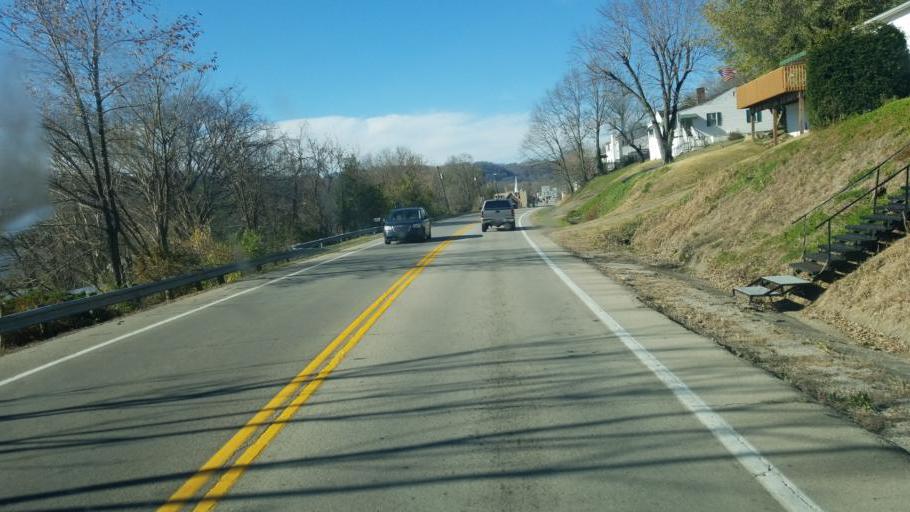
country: US
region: Ohio
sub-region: Brown County
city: Aberdeen
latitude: 38.6522
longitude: -83.7542
